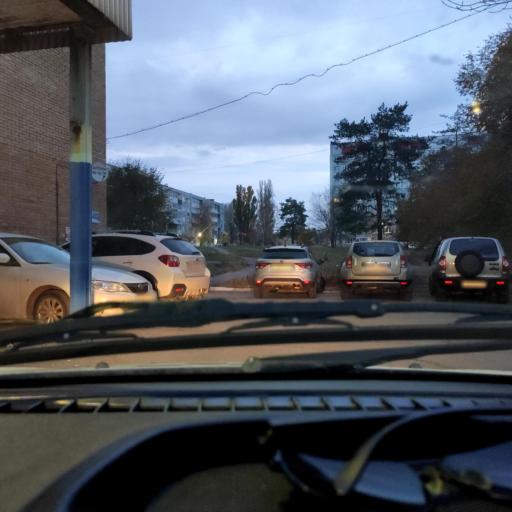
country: RU
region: Samara
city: Zhigulevsk
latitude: 53.4804
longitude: 49.4555
